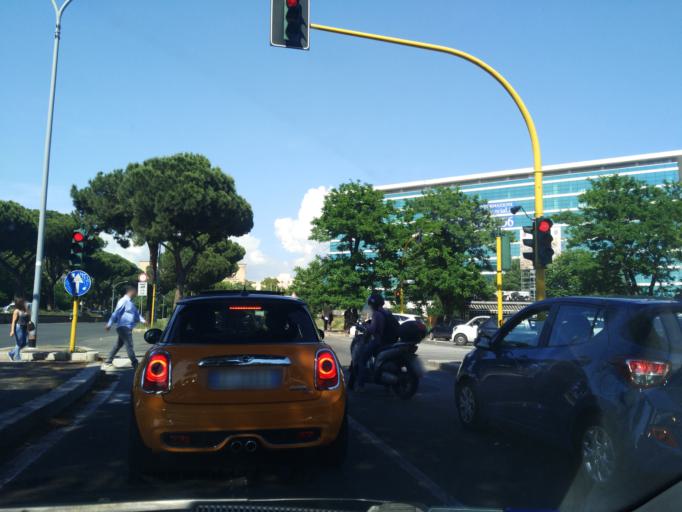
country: IT
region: Latium
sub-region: Citta metropolitana di Roma Capitale
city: Rome
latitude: 41.8583
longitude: 12.4964
